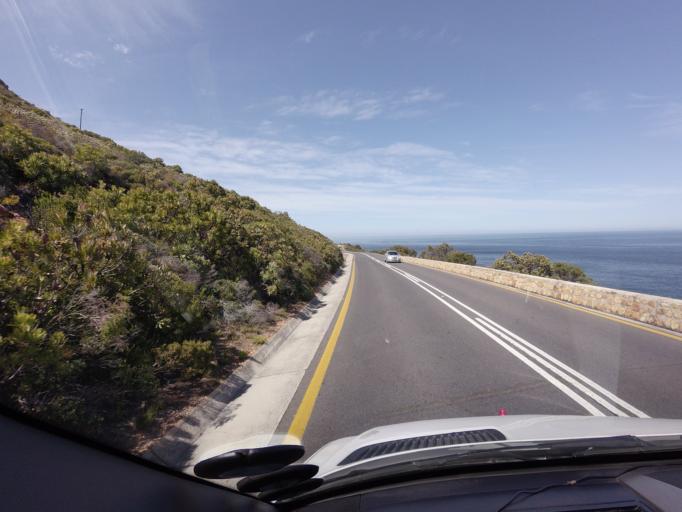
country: ZA
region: Western Cape
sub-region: Overberg District Municipality
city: Grabouw
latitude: -34.1862
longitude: 18.8203
